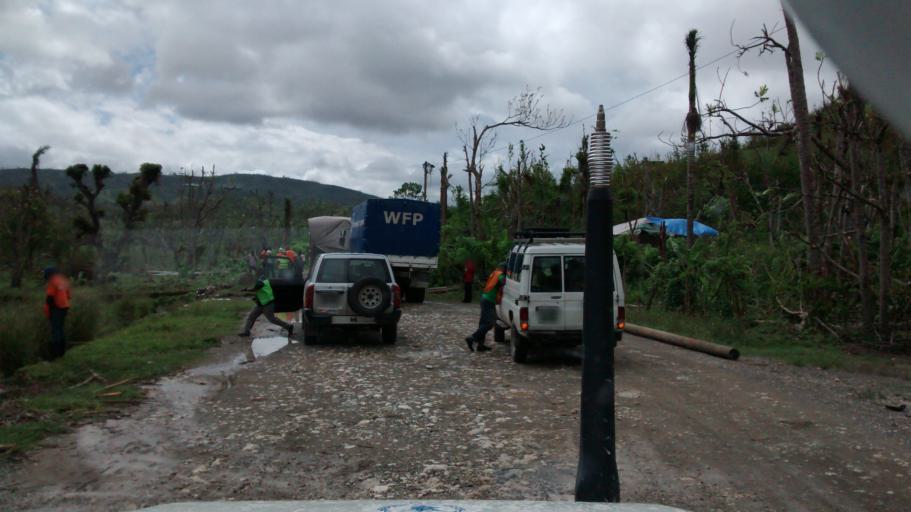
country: HT
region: Grandans
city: Jeremie
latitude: 18.5982
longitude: -74.1797
